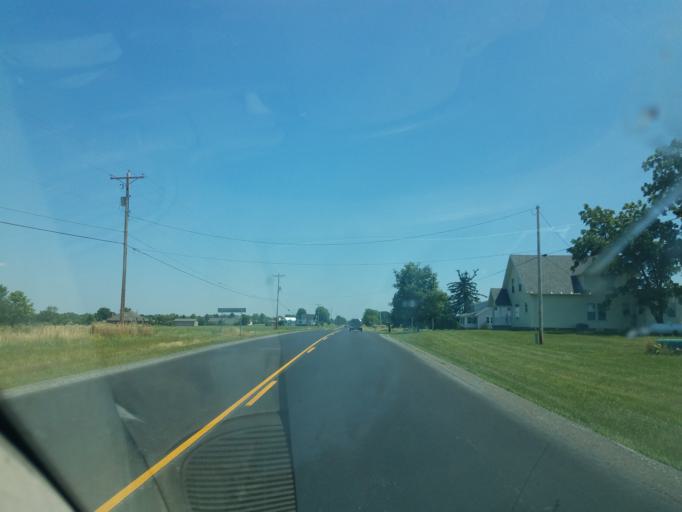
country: US
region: Ohio
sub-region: Hardin County
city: Ada
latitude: 40.7323
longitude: -83.9070
